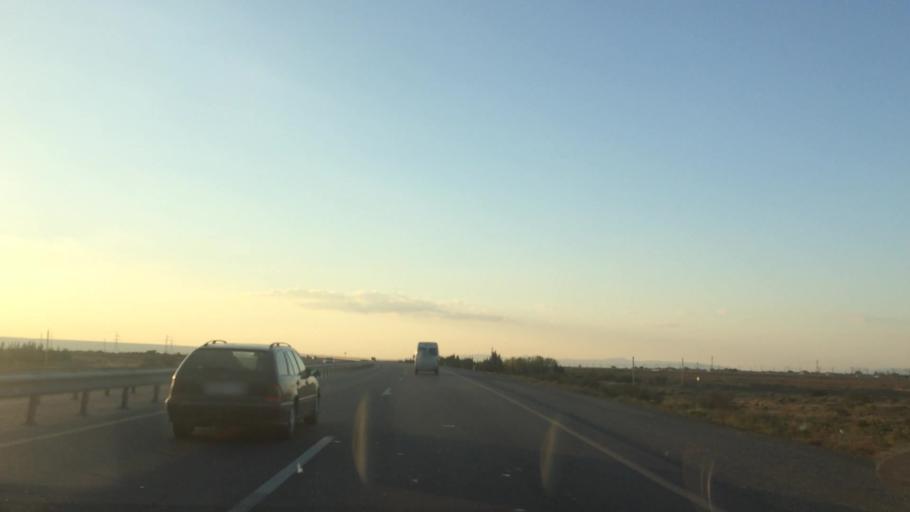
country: AZ
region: Baki
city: Qobustan
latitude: 39.9812
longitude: 49.2358
